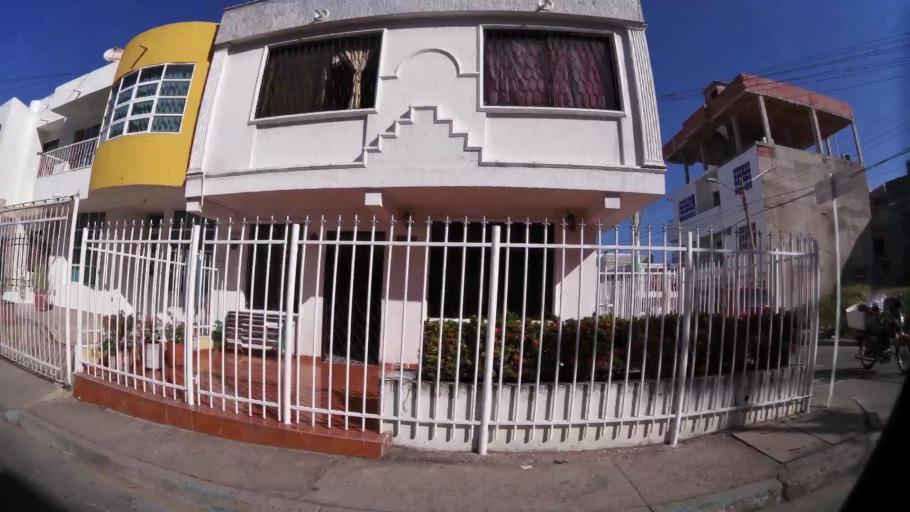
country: CO
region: Bolivar
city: Cartagena
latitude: 10.3916
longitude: -75.4945
